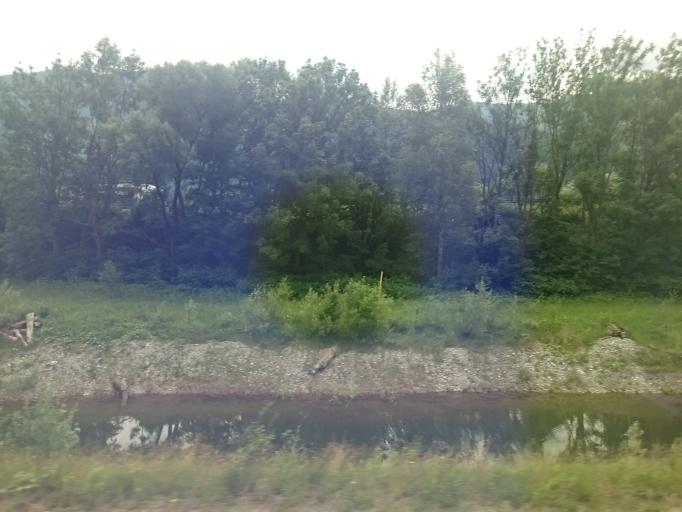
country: AT
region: Tyrol
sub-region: Politischer Bezirk Schwaz
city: Buch bei Jenbach
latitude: 47.3848
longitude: 11.7592
